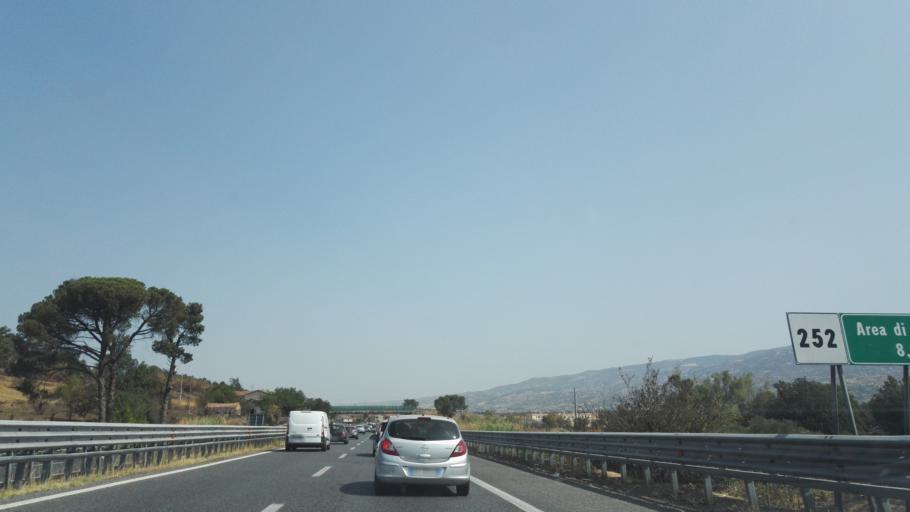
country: IT
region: Calabria
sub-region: Provincia di Cosenza
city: Quattromiglia
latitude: 39.3627
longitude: 16.2346
